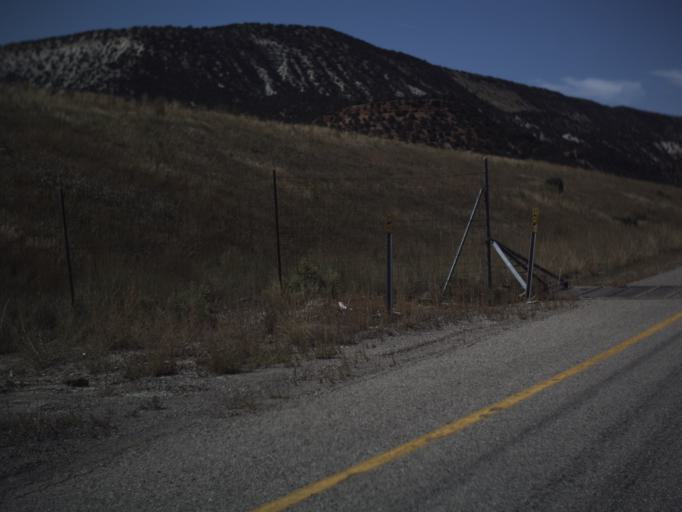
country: US
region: Utah
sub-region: Sevier County
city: Salina
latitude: 38.9170
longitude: -111.7411
